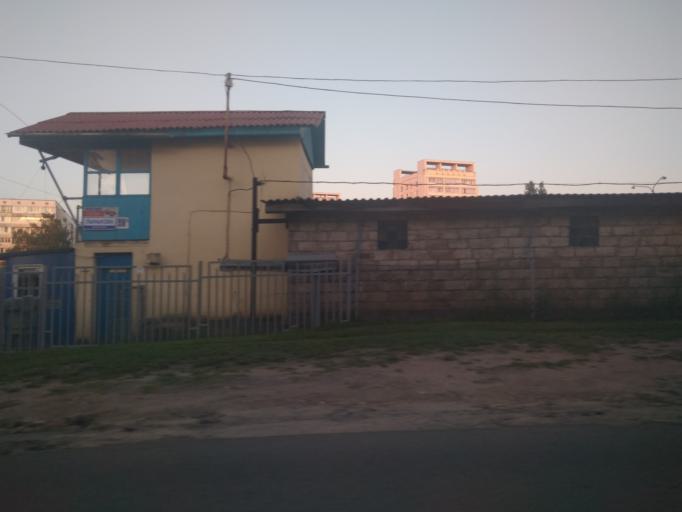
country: BY
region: Minsk
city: Novoye Medvezhino
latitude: 53.9239
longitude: 27.4736
